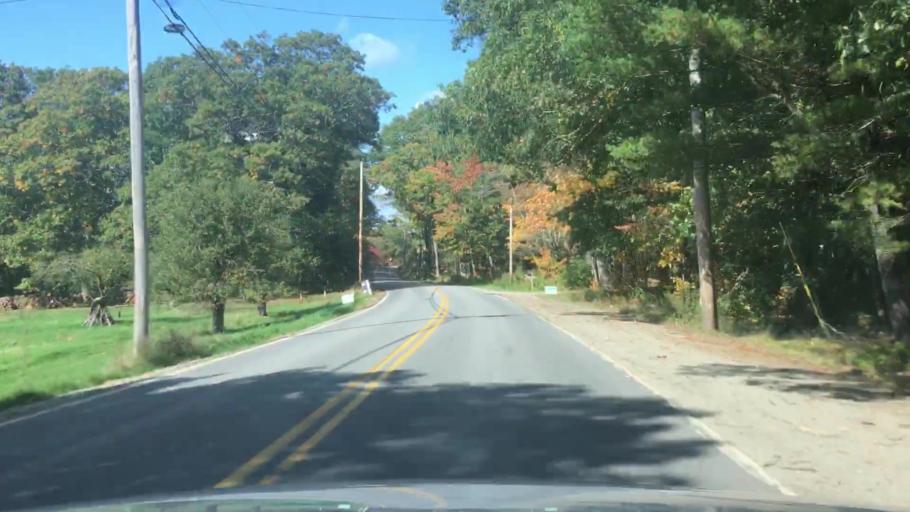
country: US
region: Maine
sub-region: Knox County
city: Warren
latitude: 44.1025
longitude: -69.2218
